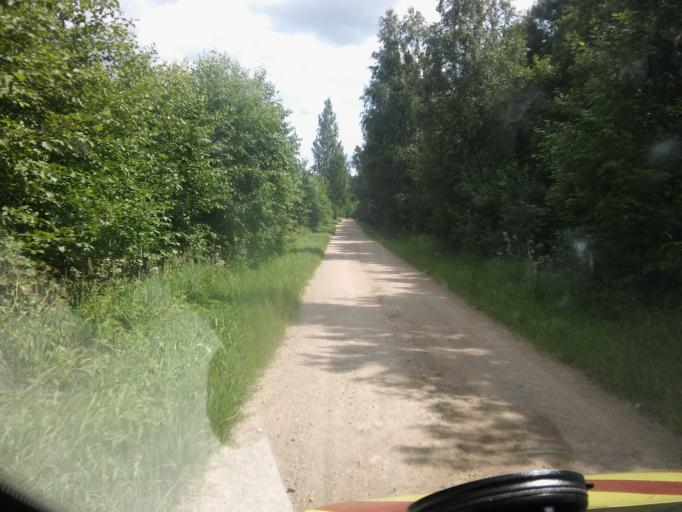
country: LV
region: Aloja
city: Staicele
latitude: 58.0427
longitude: 24.7625
